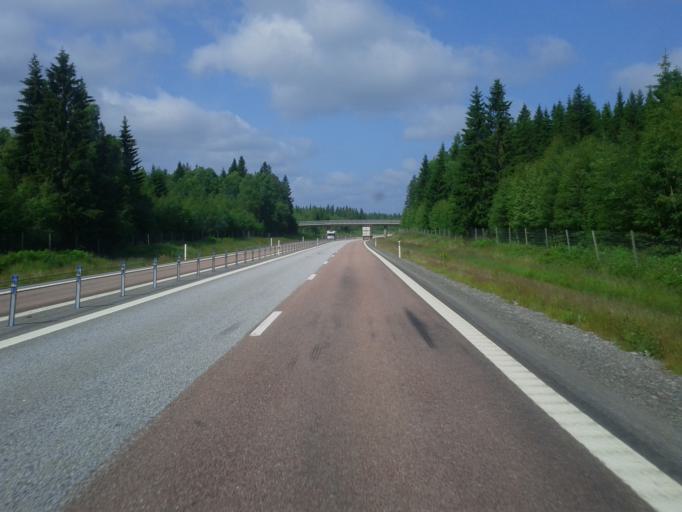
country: SE
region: Vaesterbotten
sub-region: Skelleftea Kommun
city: Soedra Bergsbyn
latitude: 64.6954
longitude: 21.0193
